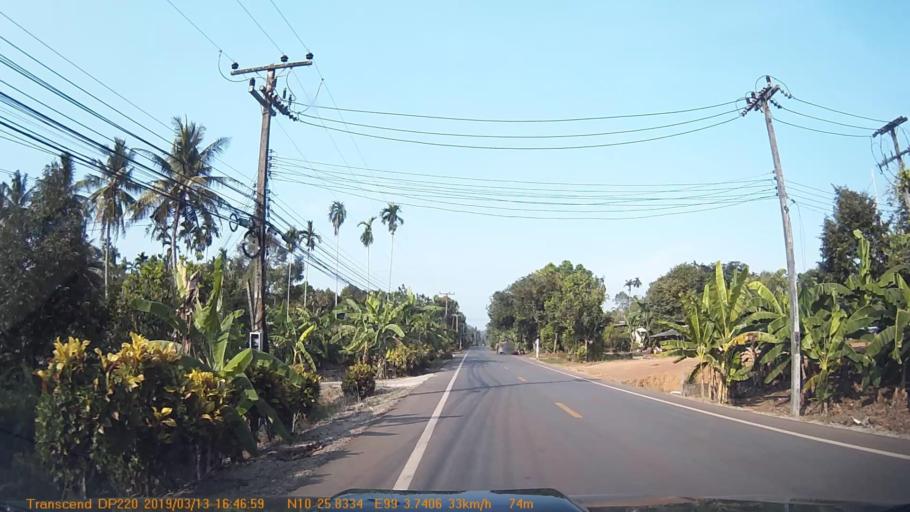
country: TH
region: Chumphon
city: Chumphon
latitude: 10.4307
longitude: 99.0625
